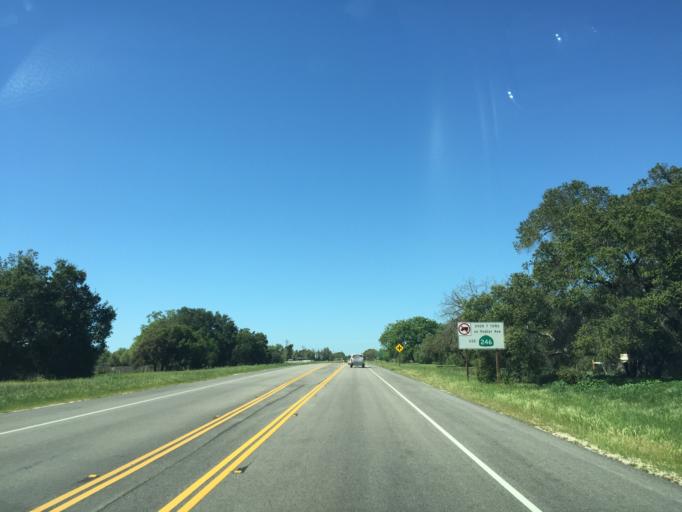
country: US
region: California
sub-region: Santa Barbara County
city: Los Olivos
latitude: 34.6481
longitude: -120.0932
